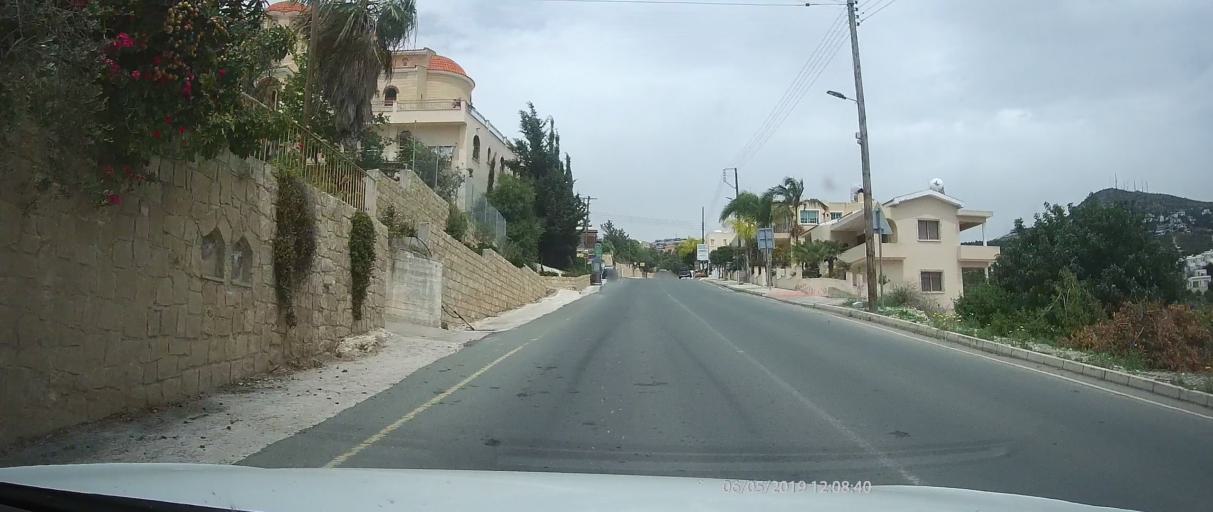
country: CY
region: Pafos
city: Tala
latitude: 34.8351
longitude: 32.4313
